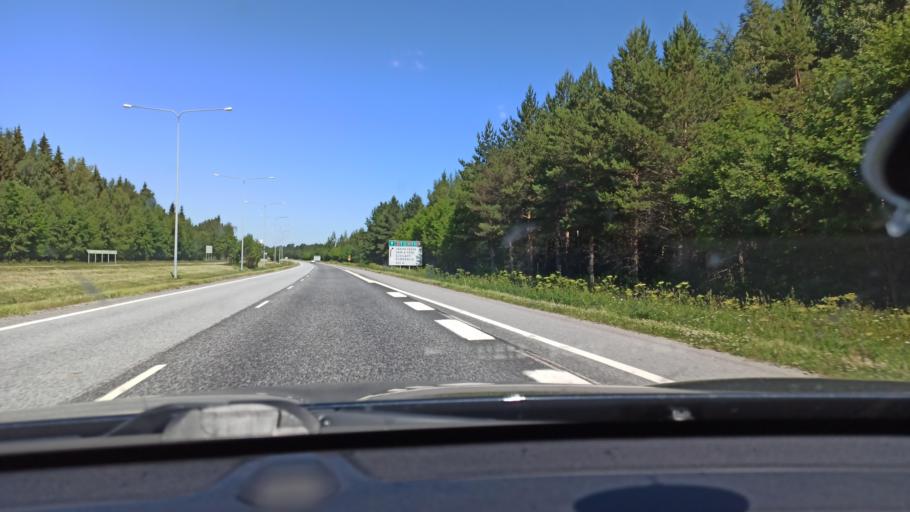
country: FI
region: Ostrobothnia
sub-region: Vaasa
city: Ristinummi
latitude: 63.0595
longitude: 21.7104
